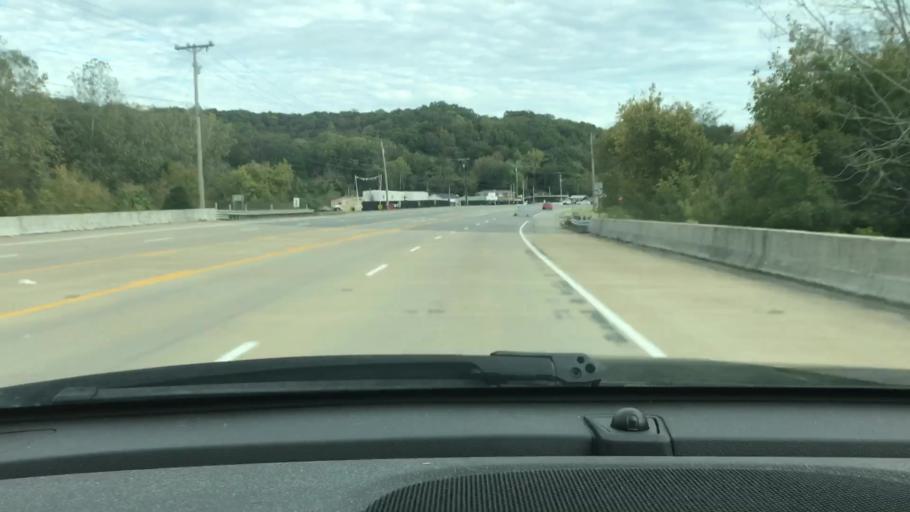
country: US
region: Tennessee
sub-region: Cheatham County
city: Ashland City
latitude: 36.2607
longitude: -87.0484
